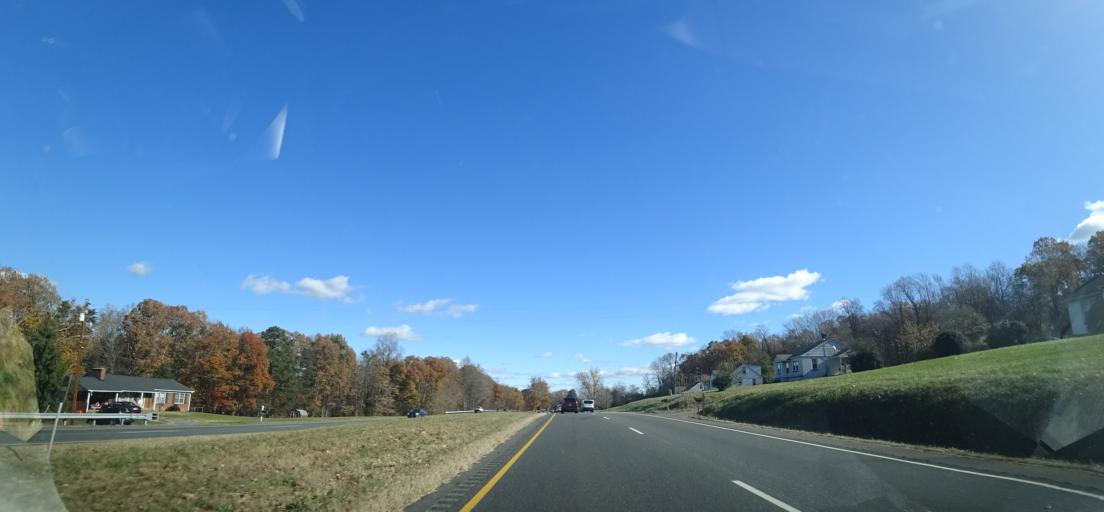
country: US
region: Virginia
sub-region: Culpeper County
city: Merrimac
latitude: 38.4518
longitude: -78.0808
